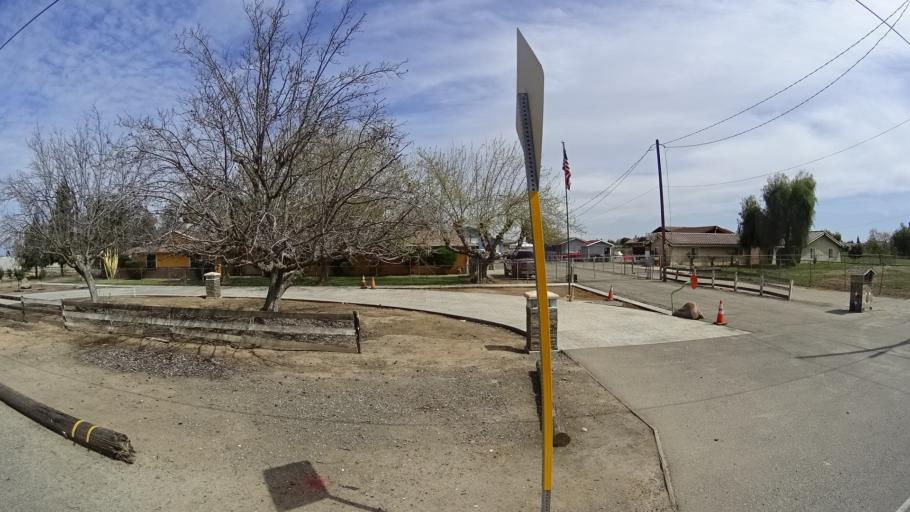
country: US
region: California
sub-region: Fresno County
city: West Park
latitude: 36.8062
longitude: -119.8985
